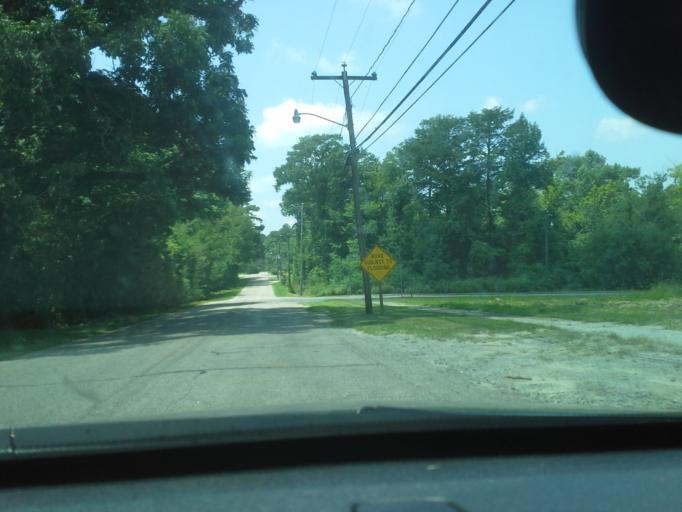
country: US
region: North Carolina
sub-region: Washington County
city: Plymouth
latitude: 35.8642
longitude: -76.7552
